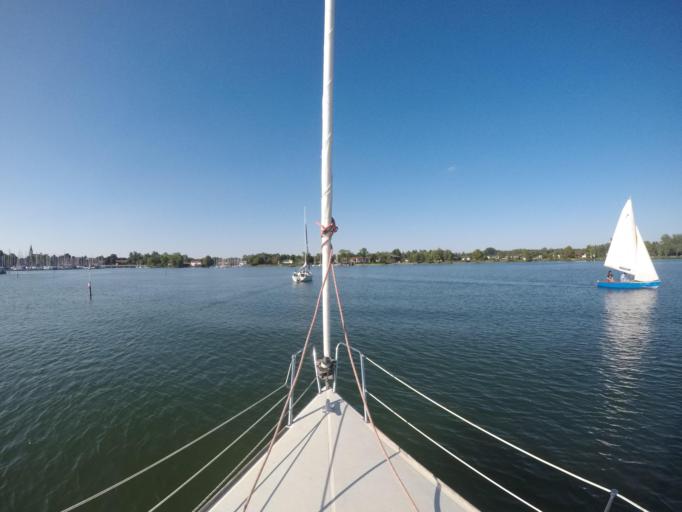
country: DE
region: Bavaria
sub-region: Upper Bavaria
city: Seeon-Seebruck
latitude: 47.9296
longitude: 12.4834
